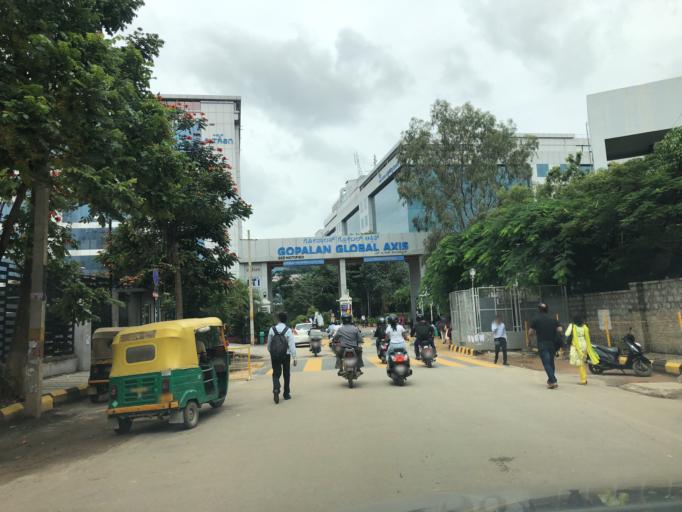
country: IN
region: Karnataka
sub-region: Bangalore Rural
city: Hoskote
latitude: 12.9821
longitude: 77.7263
